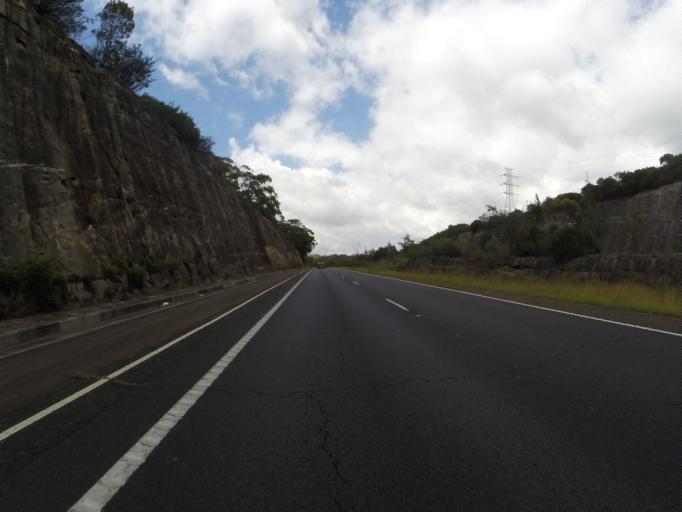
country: AU
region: New South Wales
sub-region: Wollongong
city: Helensburgh
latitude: -34.2223
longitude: 150.9523
